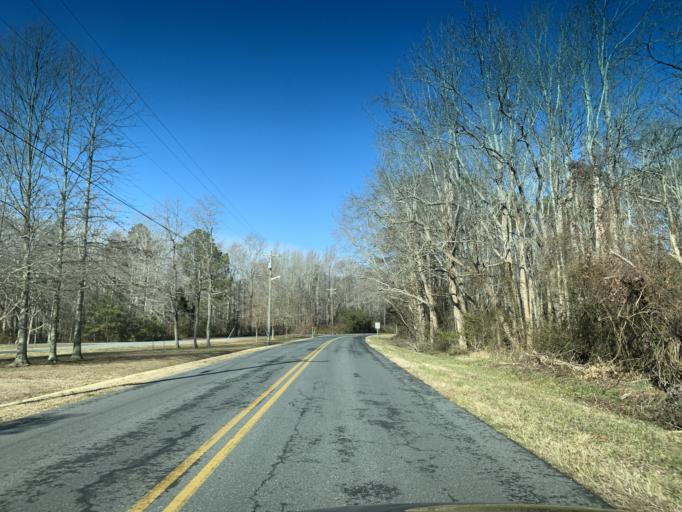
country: US
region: Maryland
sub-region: Worcester County
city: Ocean Pines
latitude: 38.3915
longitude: -75.1095
